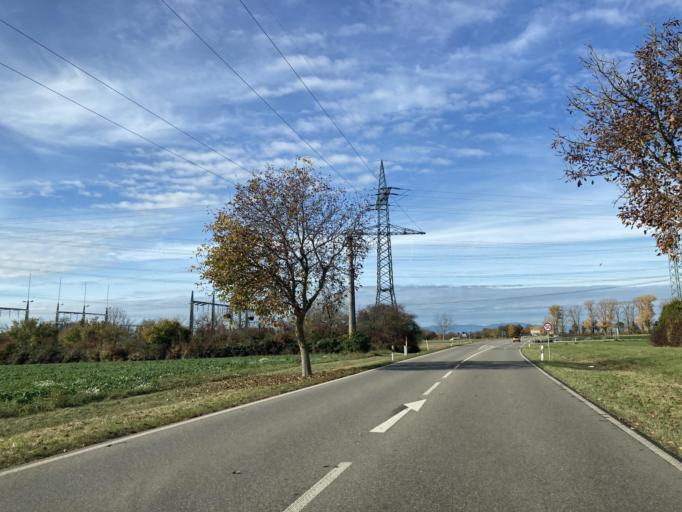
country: DE
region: Baden-Wuerttemberg
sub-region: Freiburg Region
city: Auggen
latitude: 47.8074
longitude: 7.5912
